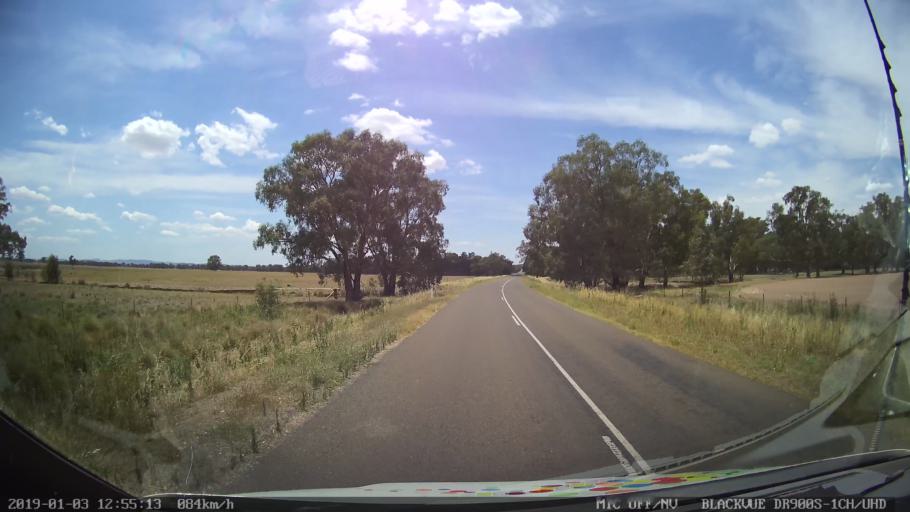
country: AU
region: New South Wales
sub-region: Weddin
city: Grenfell
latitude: -33.6464
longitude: 148.3272
